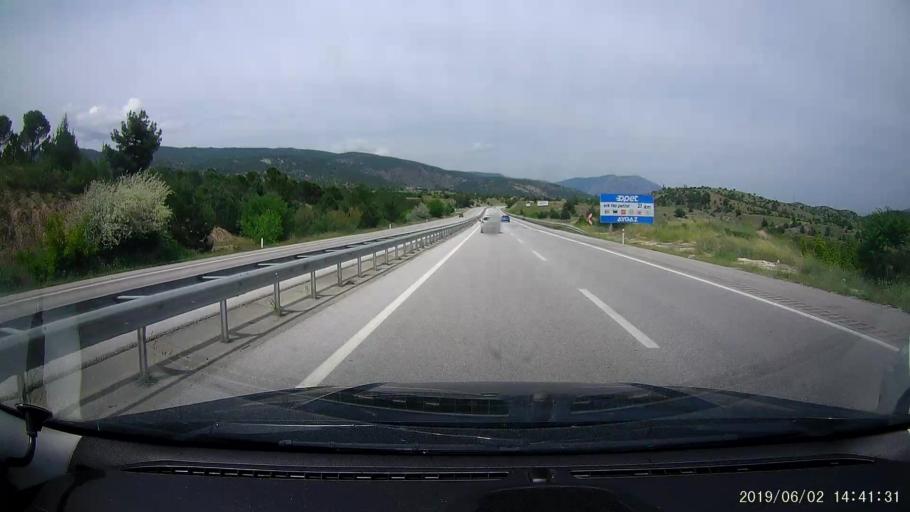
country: TR
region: Corum
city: Hacihamza
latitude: 41.0879
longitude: 34.3411
